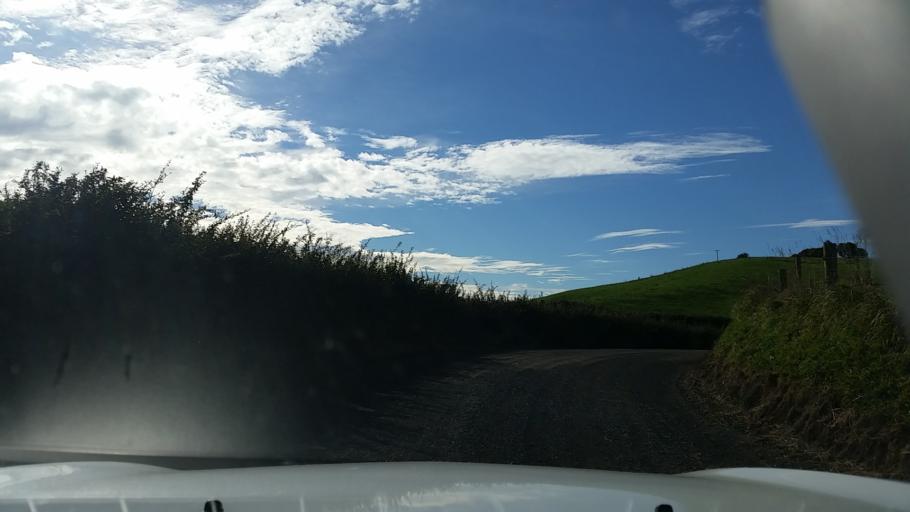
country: NZ
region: Waikato
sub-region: Matamata-Piako District
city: Matamata
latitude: -37.8207
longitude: 175.6416
